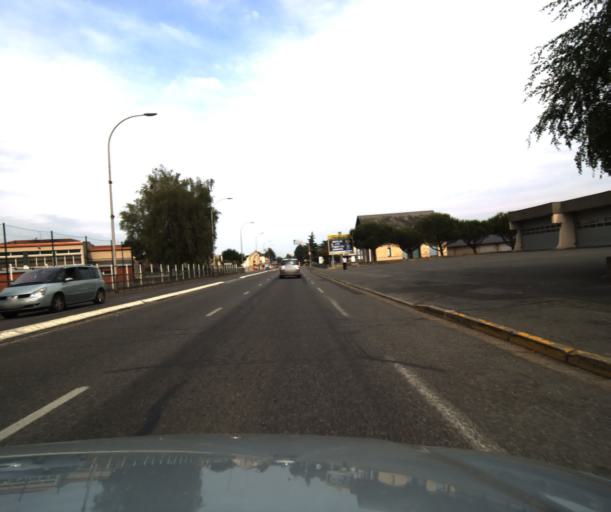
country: FR
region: Midi-Pyrenees
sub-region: Departement des Hautes-Pyrenees
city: Laloubere
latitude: 43.2199
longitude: 0.0670
